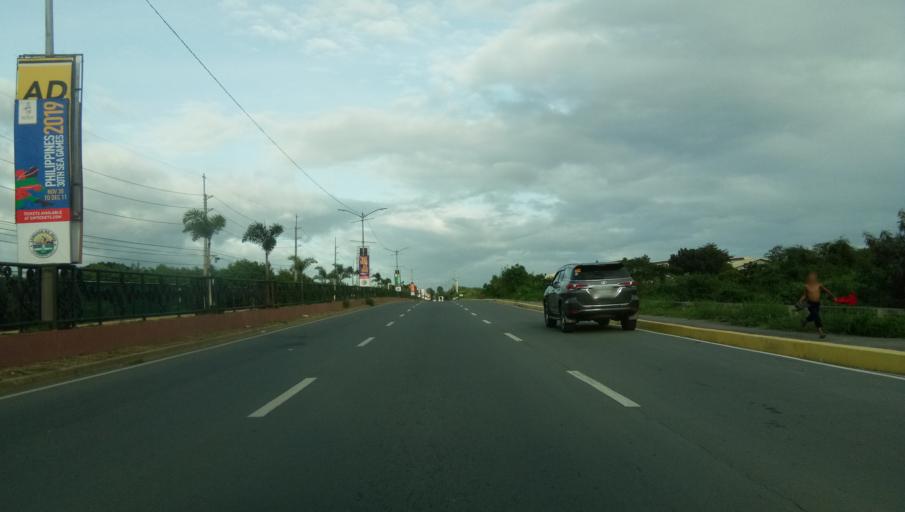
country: PH
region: Calabarzon
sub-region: Province of Cavite
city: Dasmarinas
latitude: 14.3758
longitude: 120.9475
